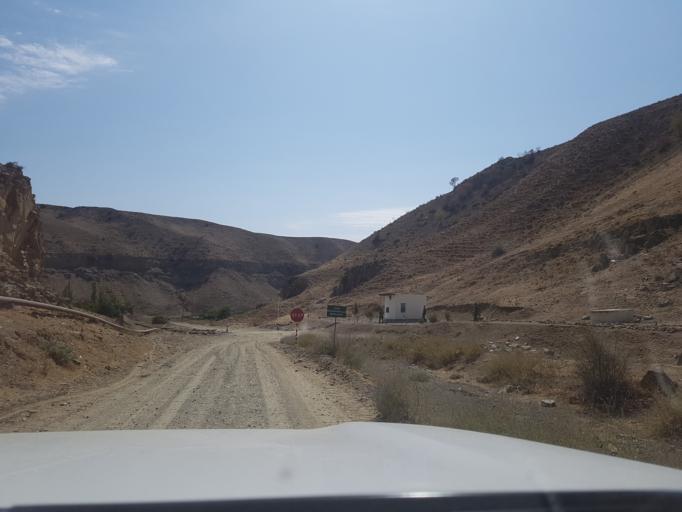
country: TM
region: Ahal
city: Baharly
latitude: 38.2373
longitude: 56.8932
